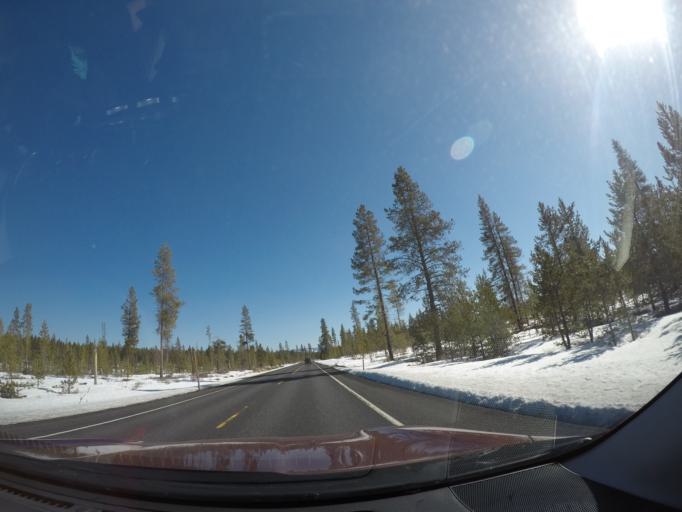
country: US
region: Oregon
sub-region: Deschutes County
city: Three Rivers
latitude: 43.8637
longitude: -121.5350
